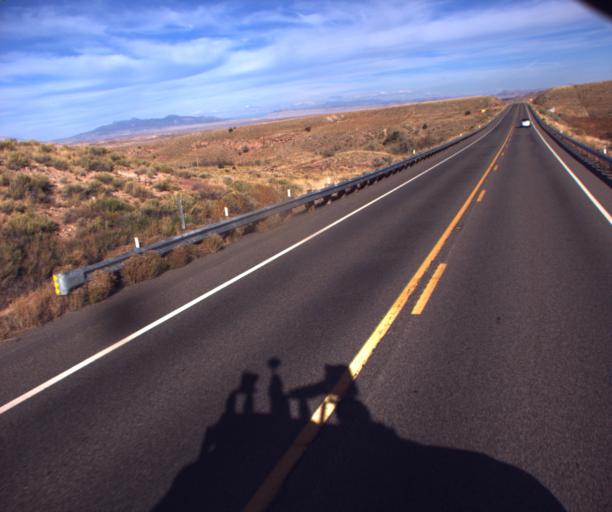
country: US
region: New Mexico
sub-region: San Juan County
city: Shiprock
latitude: 36.9270
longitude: -109.1693
